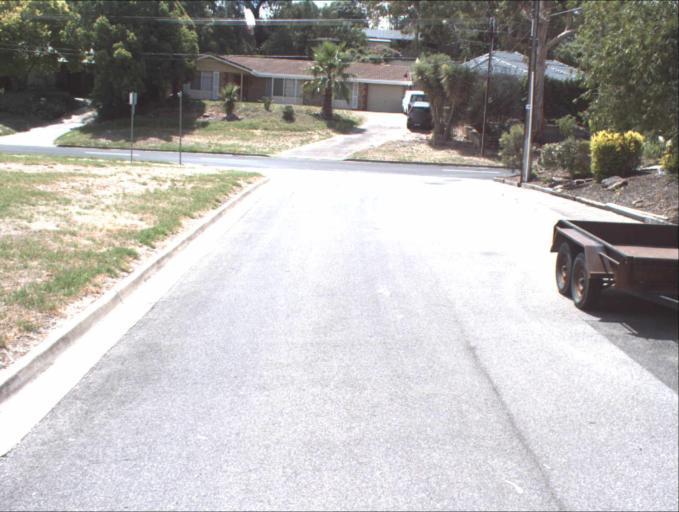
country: AU
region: South Australia
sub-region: Port Adelaide Enfield
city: Gilles Plains
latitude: -34.8404
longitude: 138.6585
